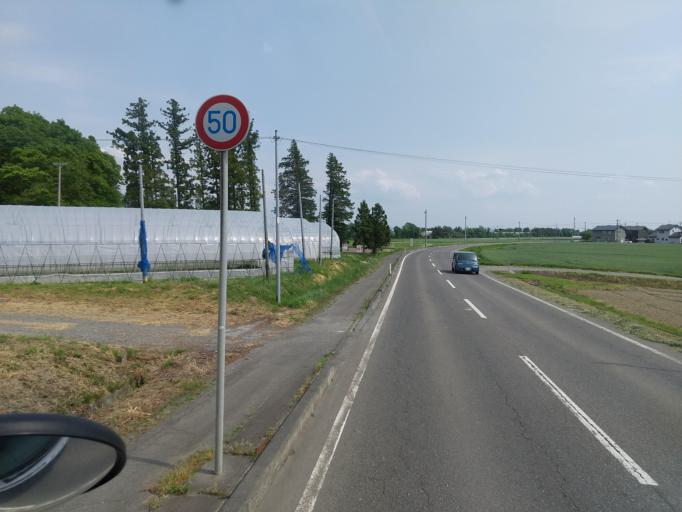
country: JP
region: Iwate
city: Hanamaki
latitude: 39.3972
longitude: 141.0894
